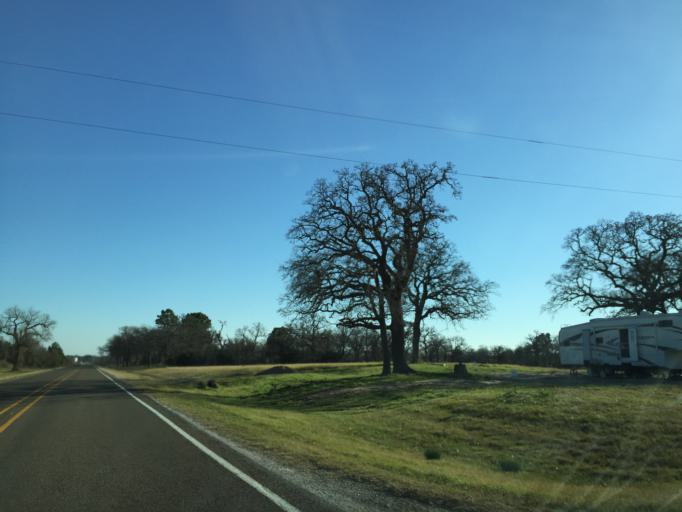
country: US
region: Texas
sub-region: Bastrop County
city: Elgin
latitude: 30.3968
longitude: -97.2481
